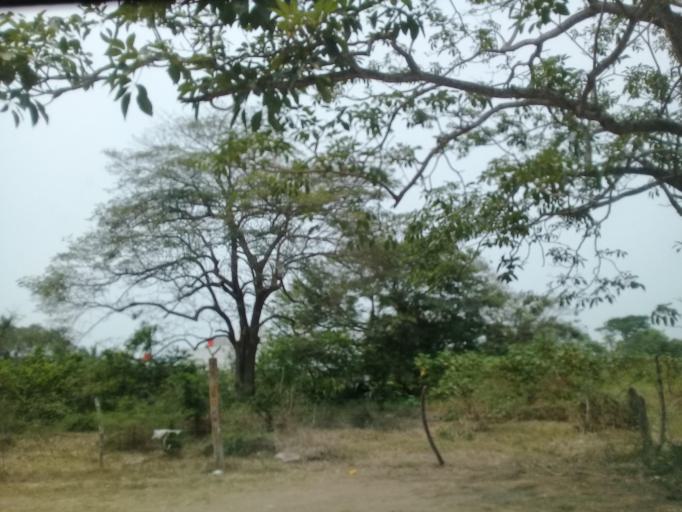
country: MX
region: Veracruz
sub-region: Veracruz
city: Lomas de Rio Medio Cuatro
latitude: 19.1753
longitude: -96.2090
